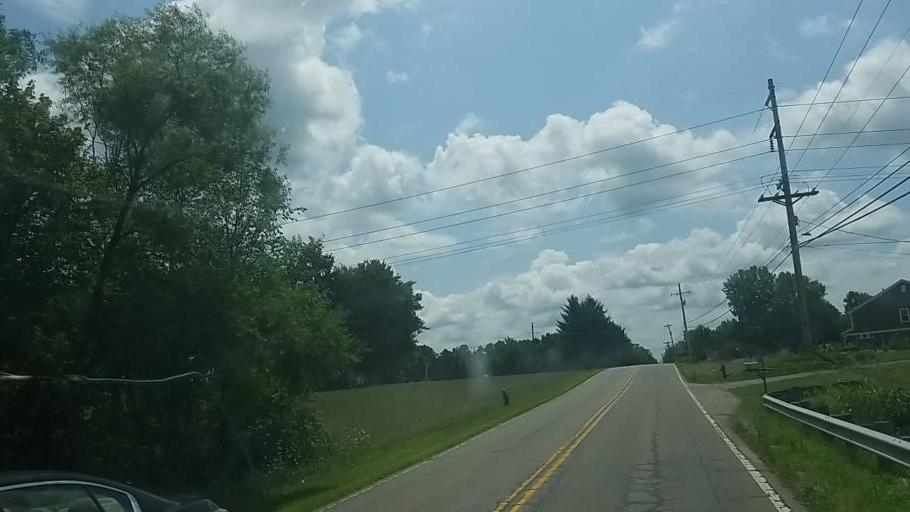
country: US
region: Ohio
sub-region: Fairfield County
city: Pickerington
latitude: 39.9014
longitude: -82.7480
